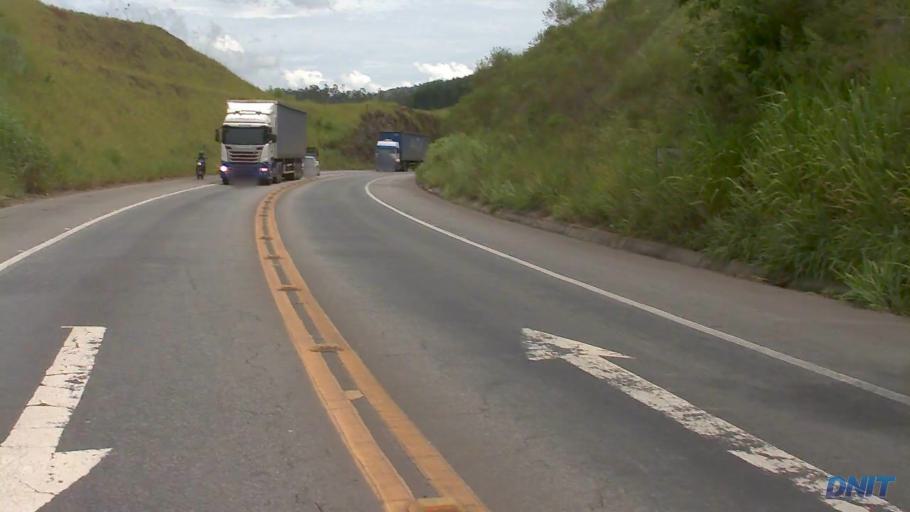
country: BR
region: Minas Gerais
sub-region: Coronel Fabriciano
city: Coronel Fabriciano
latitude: -19.5304
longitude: -42.6039
